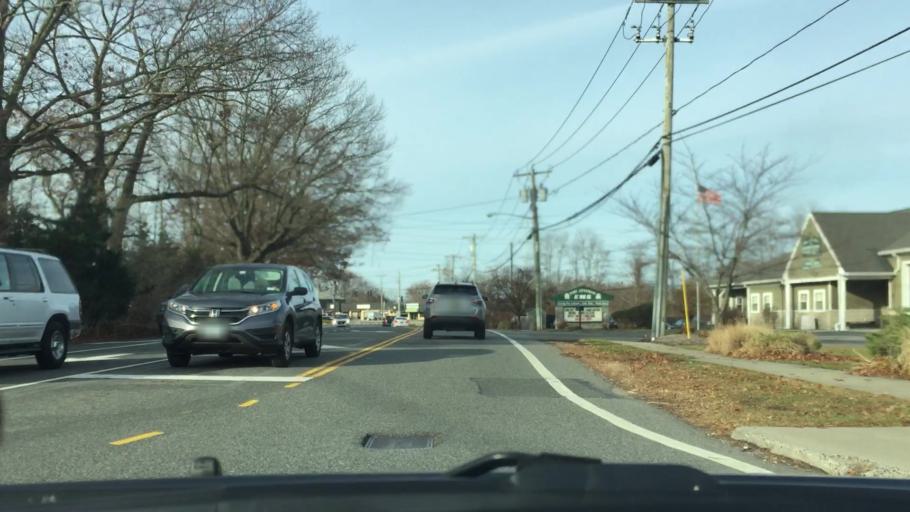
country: US
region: New York
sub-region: Suffolk County
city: Port Jefferson Station
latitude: 40.9318
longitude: -73.0351
